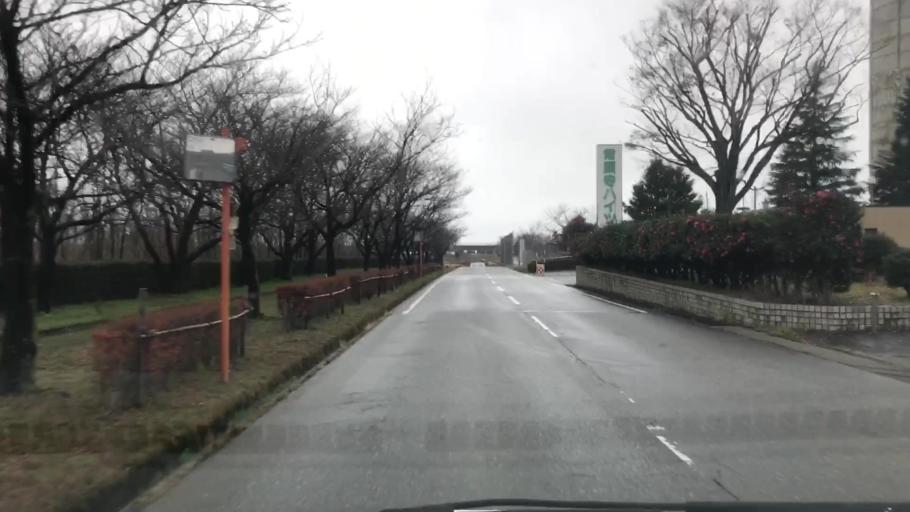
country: JP
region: Toyama
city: Kamiichi
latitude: 36.6238
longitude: 137.3024
